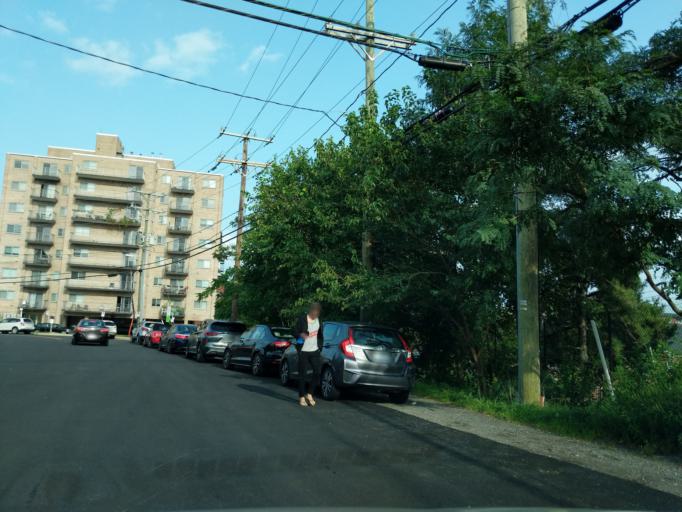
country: US
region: Virginia
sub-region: Arlington County
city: Arlington
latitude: 38.8876
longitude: -77.0764
